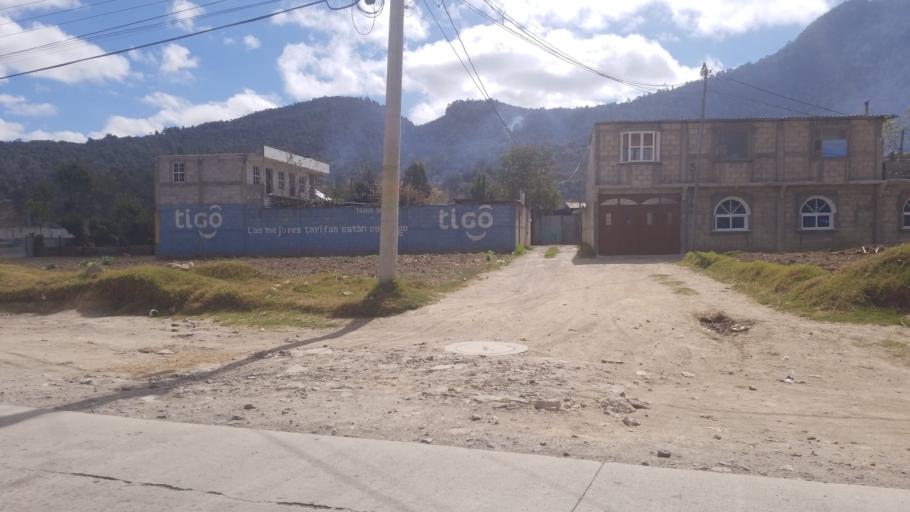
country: GT
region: Quetzaltenango
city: Quetzaltenango
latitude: 14.8103
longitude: -91.5398
